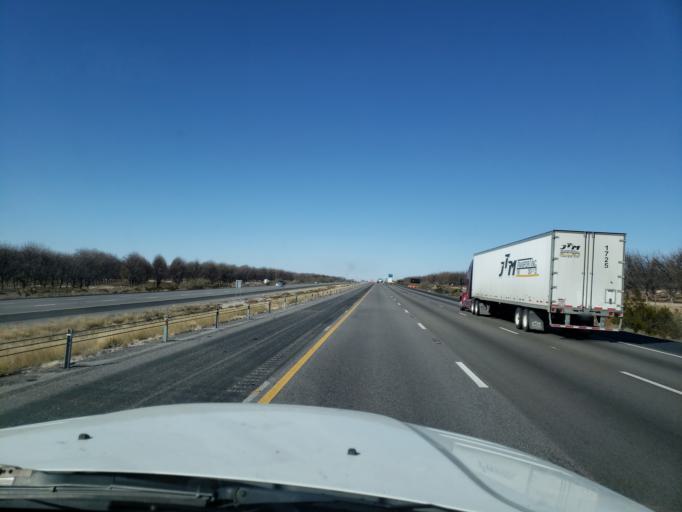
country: US
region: New Mexico
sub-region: Dona Ana County
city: University Park
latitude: 32.2322
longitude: -106.7116
